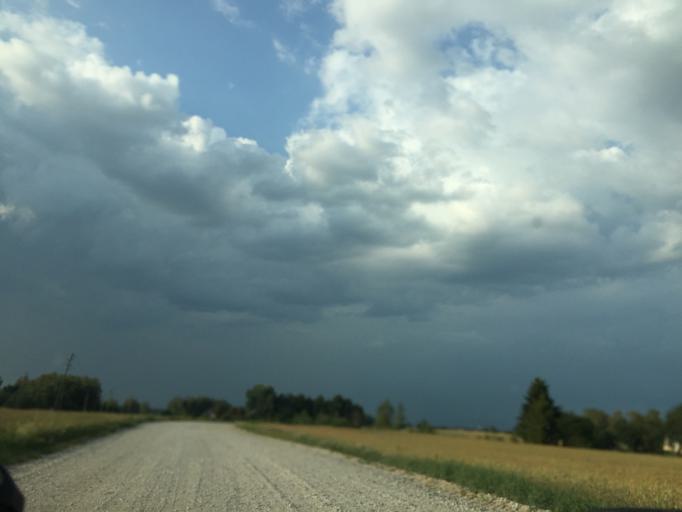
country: LV
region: Dobeles Rajons
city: Dobele
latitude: 56.5875
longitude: 23.3069
